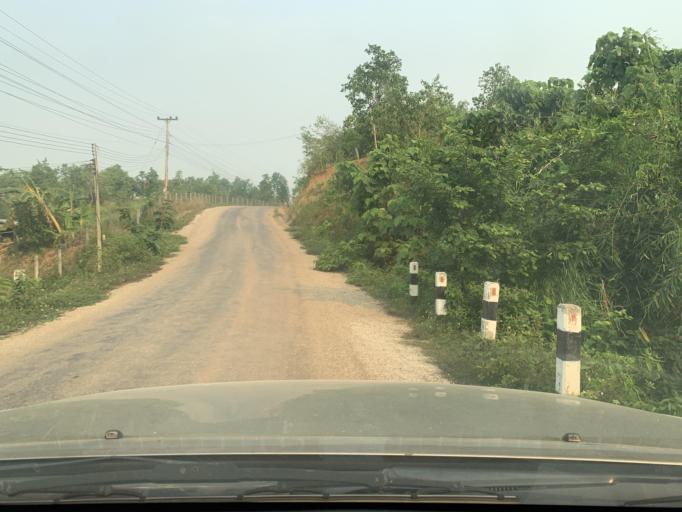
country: LA
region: Louangphabang
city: Louangphabang
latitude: 19.9098
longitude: 102.0827
